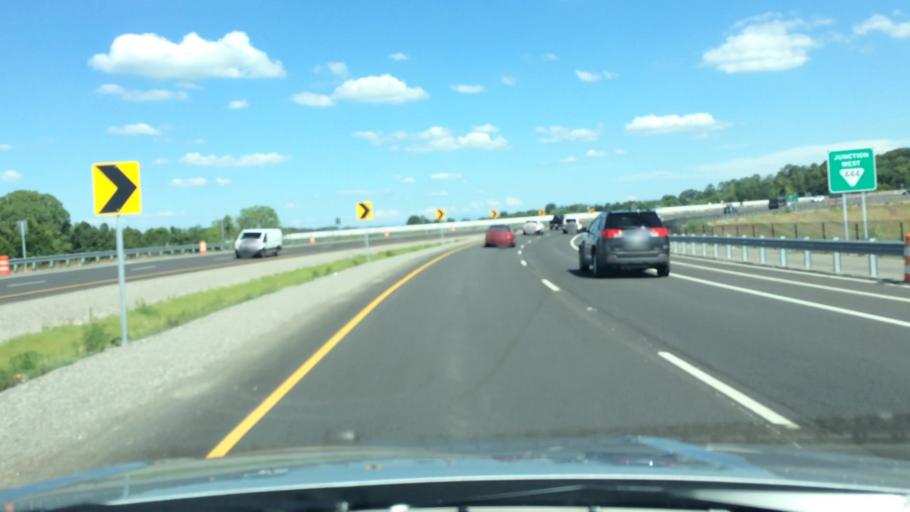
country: US
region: Tennessee
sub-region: Loudon County
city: Lenoir City
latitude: 35.7859
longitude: -84.2450
